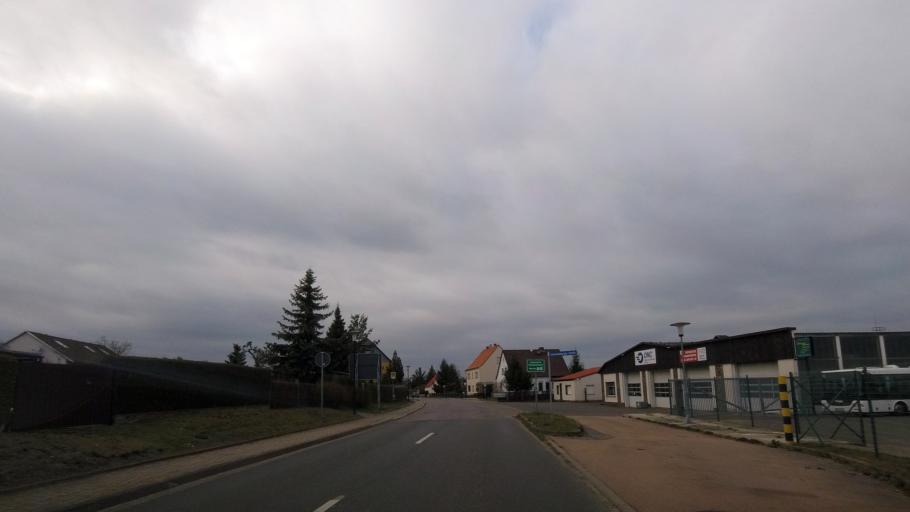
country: DE
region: Saxony-Anhalt
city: Kemberg
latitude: 51.7653
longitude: 12.6379
